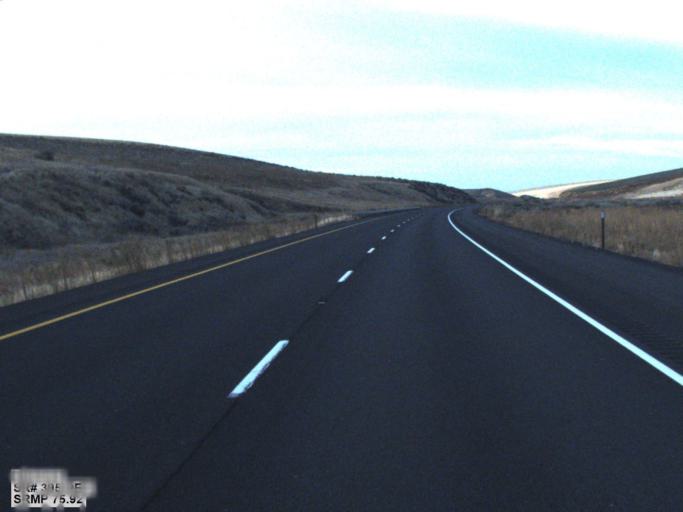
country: US
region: Washington
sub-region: Franklin County
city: Connell
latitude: 46.8873
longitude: -118.6174
